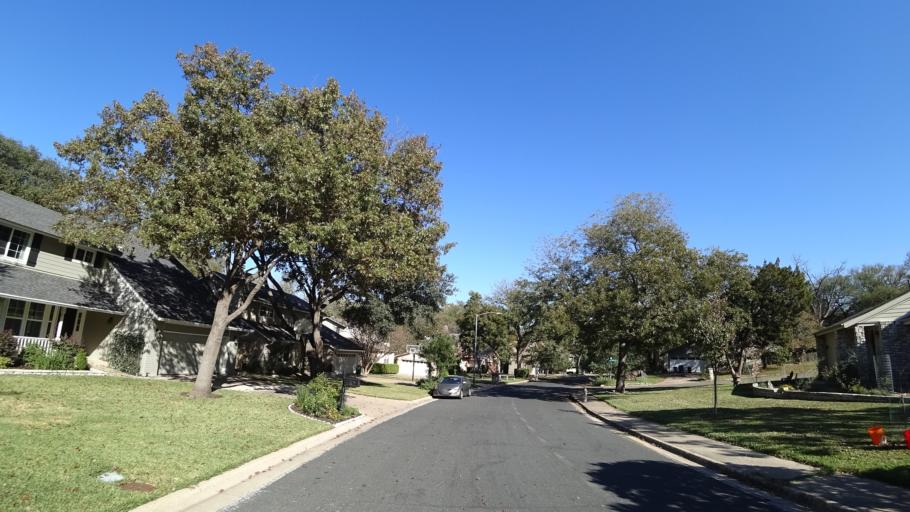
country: US
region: Texas
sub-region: Williamson County
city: Jollyville
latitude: 30.4220
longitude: -97.7690
